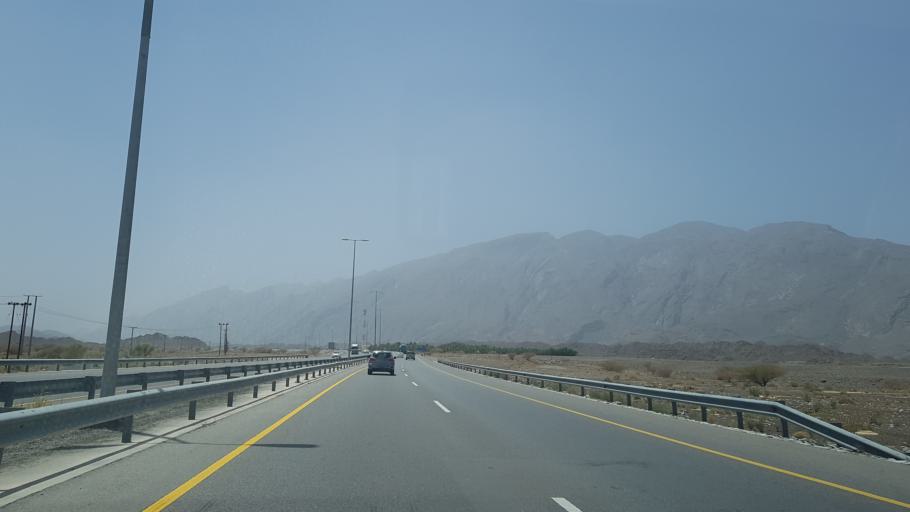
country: OM
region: Muhafazat ad Dakhiliyah
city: Sufalat Sama'il
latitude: 23.2513
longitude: 57.9243
